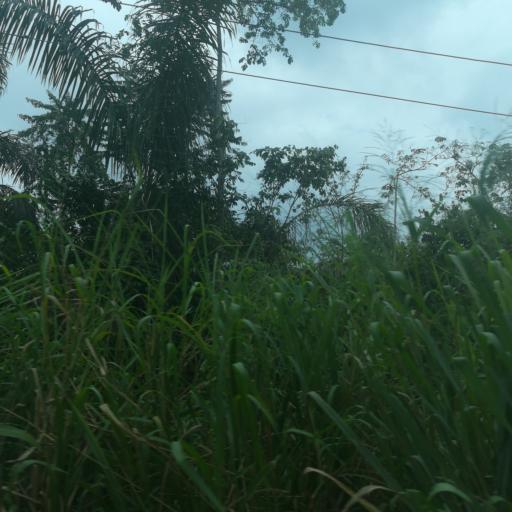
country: NG
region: Lagos
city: Ejirin
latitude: 6.6627
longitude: 3.8127
